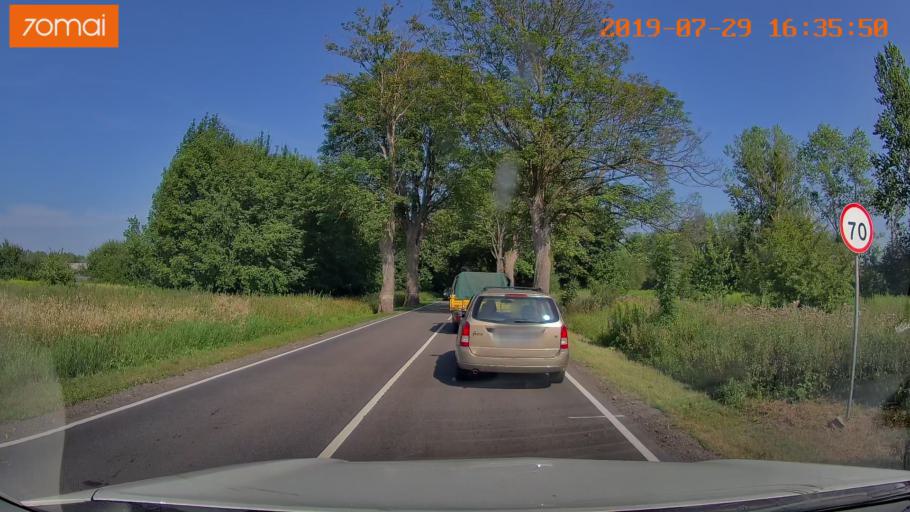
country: RU
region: Kaliningrad
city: Primorsk
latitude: 54.7402
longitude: 20.0596
